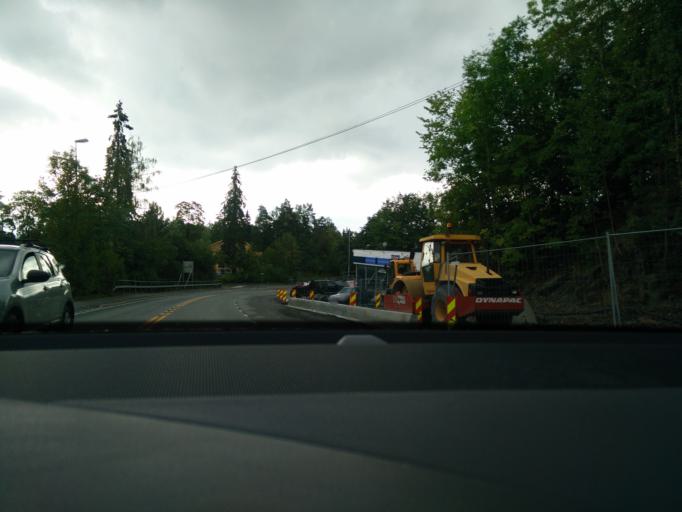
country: NO
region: Akershus
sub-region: Baerum
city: Lysaker
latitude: 59.9294
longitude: 10.6209
